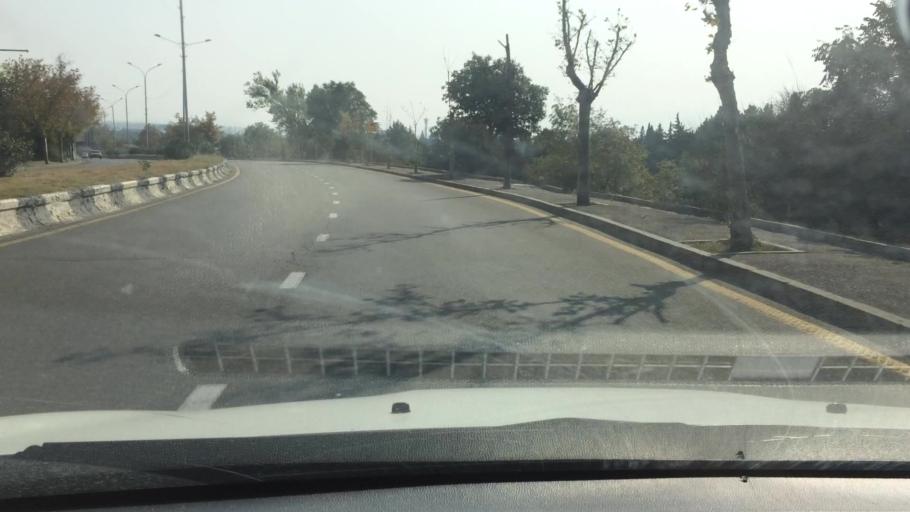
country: GE
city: Didi Lilo
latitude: 41.6853
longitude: 44.9532
